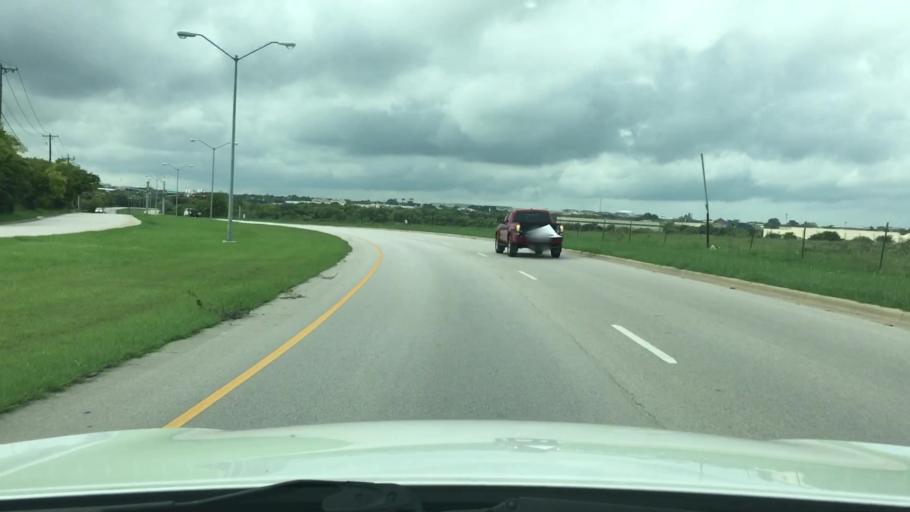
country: US
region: Texas
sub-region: Travis County
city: Windemere
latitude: 30.4792
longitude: -97.6652
